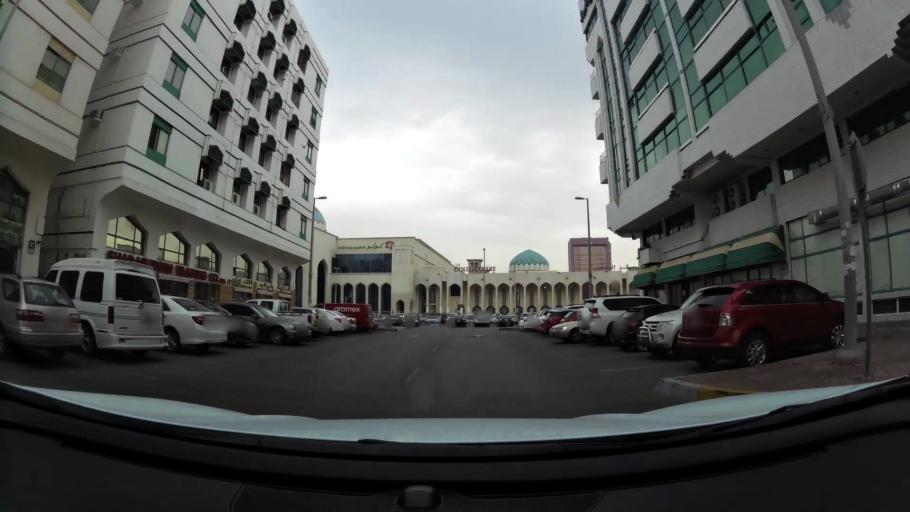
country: AE
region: Abu Dhabi
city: Abu Dhabi
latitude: 24.4815
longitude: 54.3648
